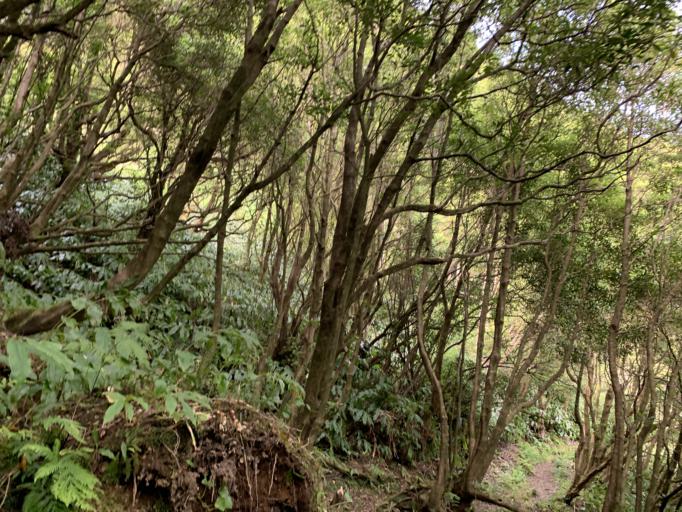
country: PT
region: Azores
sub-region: Ponta Delgada
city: Arrifes
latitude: 37.8527
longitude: -25.7742
